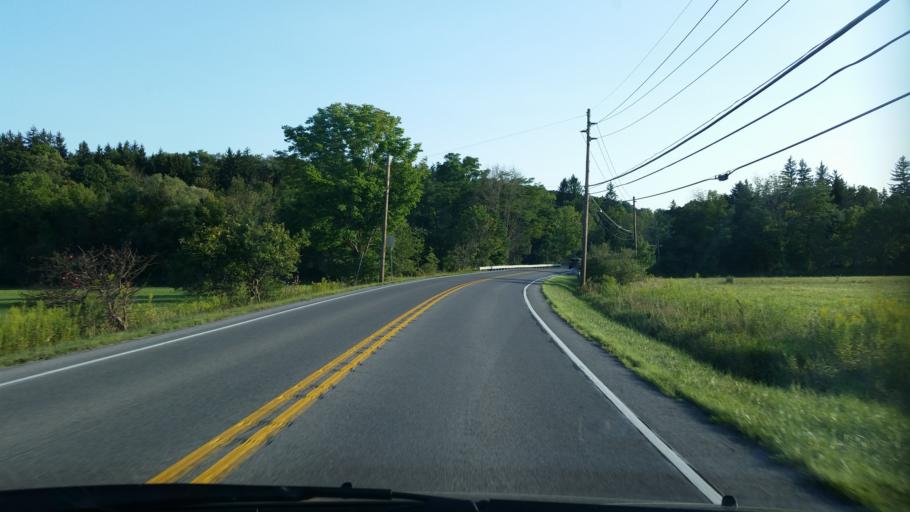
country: US
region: Pennsylvania
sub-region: Blair County
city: Greenwood
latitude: 40.5758
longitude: -78.3705
